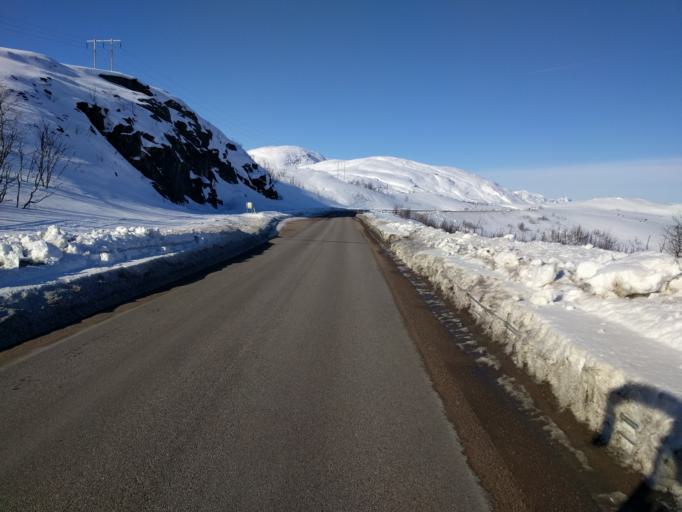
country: NO
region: Troms
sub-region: Bardu
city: Setermoen
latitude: 68.4310
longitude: 18.2137
